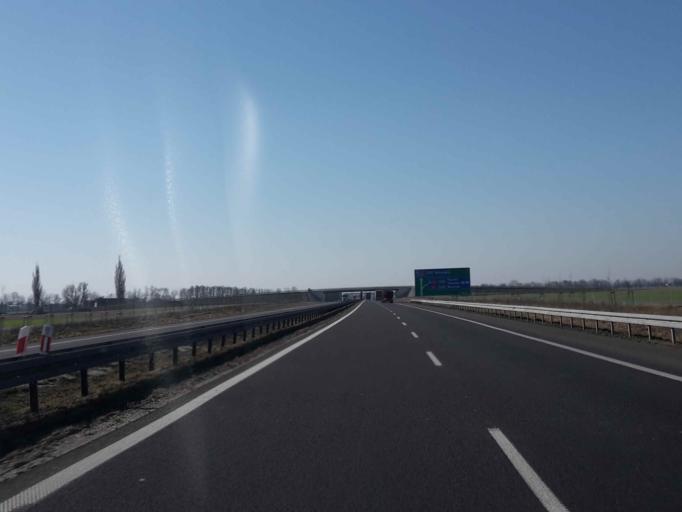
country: PL
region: Greater Poland Voivodeship
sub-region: Powiat poznanski
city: Kleszczewo
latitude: 52.3330
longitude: 17.1513
